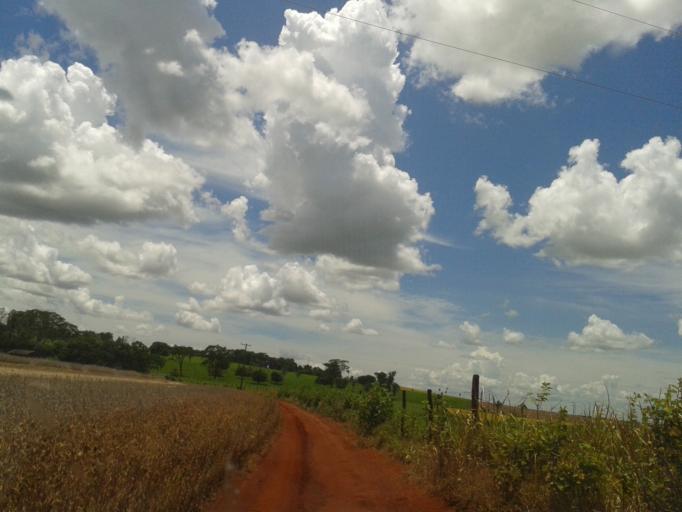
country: BR
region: Minas Gerais
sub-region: Capinopolis
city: Capinopolis
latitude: -18.7623
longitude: -49.7905
